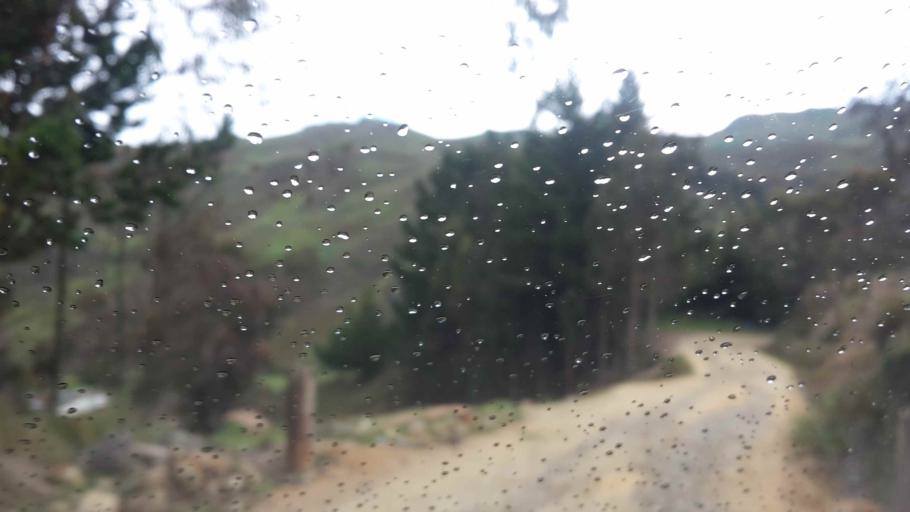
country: BO
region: Cochabamba
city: Cochabamba
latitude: -17.1360
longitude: -66.1058
